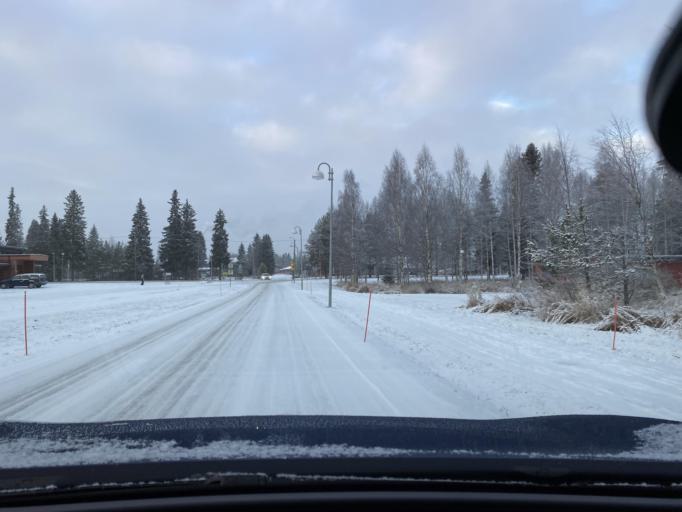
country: FI
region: Lapland
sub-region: Rovaniemi
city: Ranua
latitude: 65.9263
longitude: 26.5154
